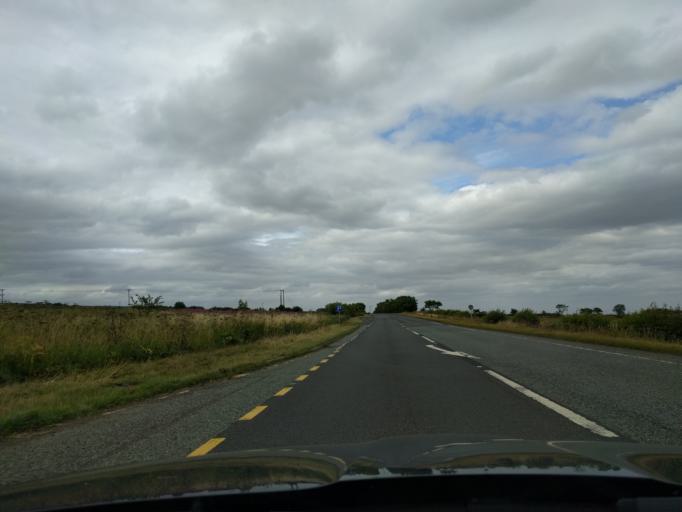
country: GB
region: England
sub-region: Northumberland
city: Ellingham
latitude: 55.5193
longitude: -1.7467
